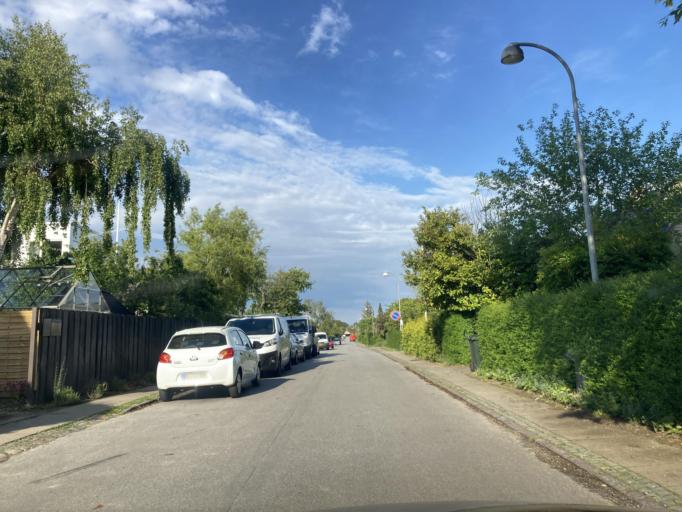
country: DK
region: Capital Region
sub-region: Hvidovre Kommune
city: Hvidovre
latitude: 55.6398
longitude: 12.4798
